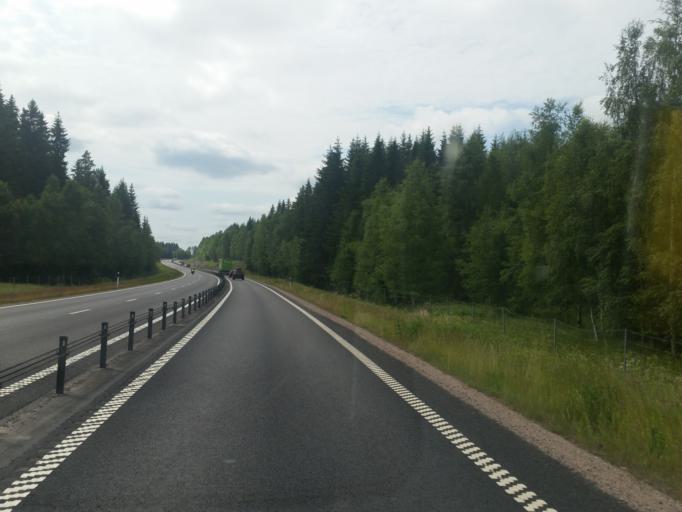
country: SE
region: Dalarna
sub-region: Borlange Kommun
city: Borlaenge
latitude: 60.4544
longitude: 15.3715
